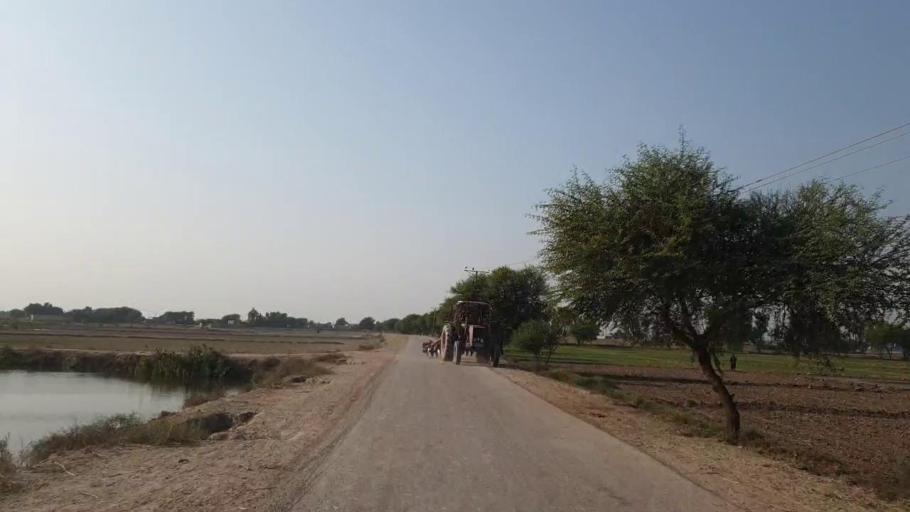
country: PK
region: Sindh
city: Bulri
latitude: 24.9958
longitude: 68.3821
